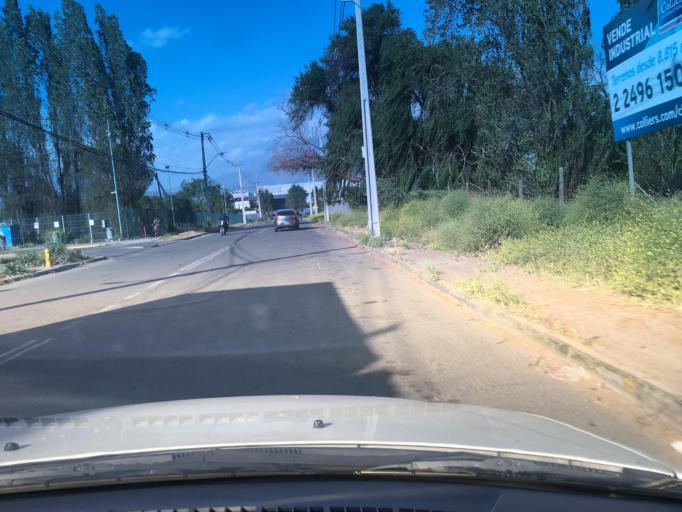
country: CL
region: Santiago Metropolitan
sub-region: Provincia de Chacabuco
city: Chicureo Abajo
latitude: -33.3082
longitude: -70.7182
